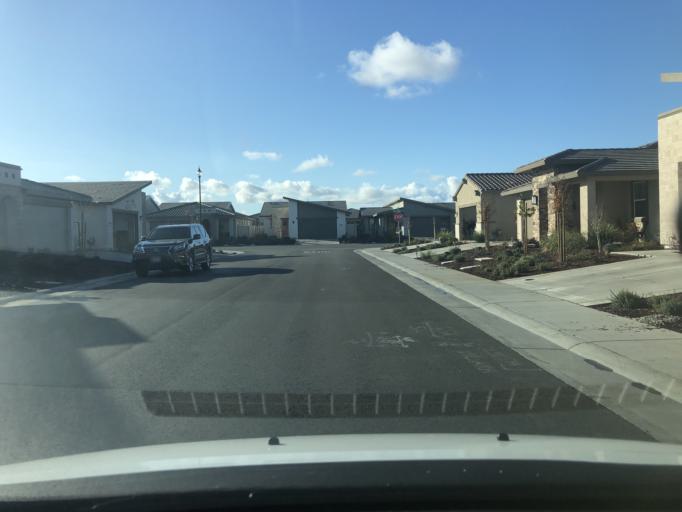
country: US
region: California
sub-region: Sacramento County
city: Antelope
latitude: 38.7722
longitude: -121.3874
